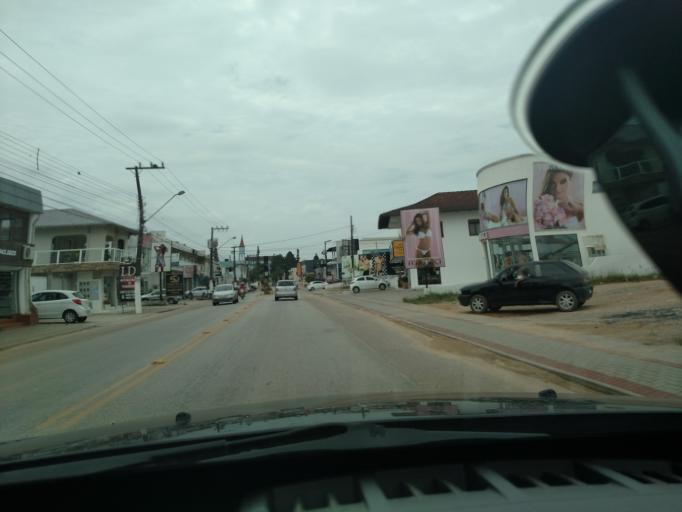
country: BR
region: Santa Catarina
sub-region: Gaspar
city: Gaspar
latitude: -26.9032
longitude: -48.8309
